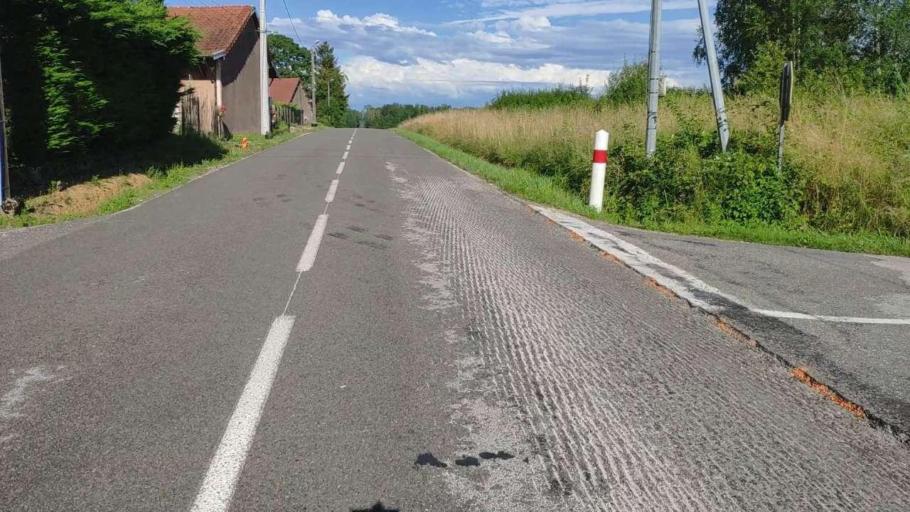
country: FR
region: Franche-Comte
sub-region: Departement du Jura
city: Bletterans
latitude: 46.8263
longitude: 5.5119
